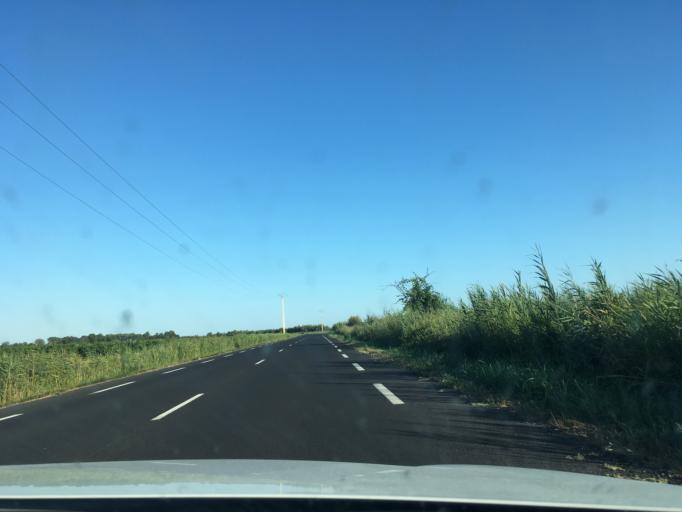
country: FR
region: Languedoc-Roussillon
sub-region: Departement du Gard
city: Aigues-Mortes
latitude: 43.5662
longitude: 4.3130
